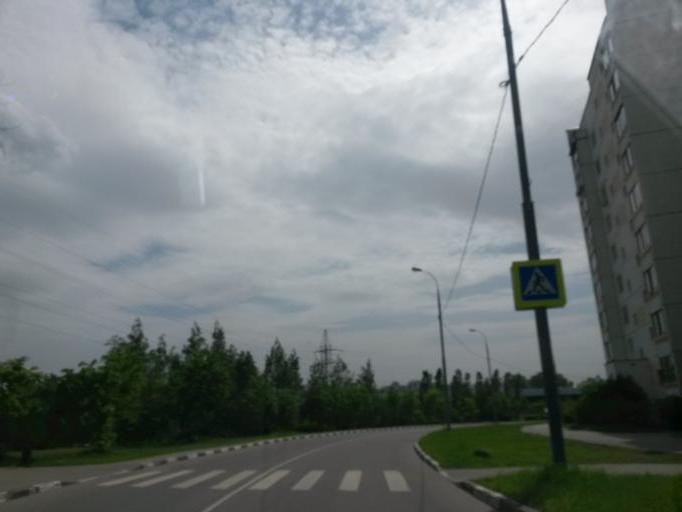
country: RU
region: Moskovskaya
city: Kommunarka
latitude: 55.5430
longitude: 37.5278
